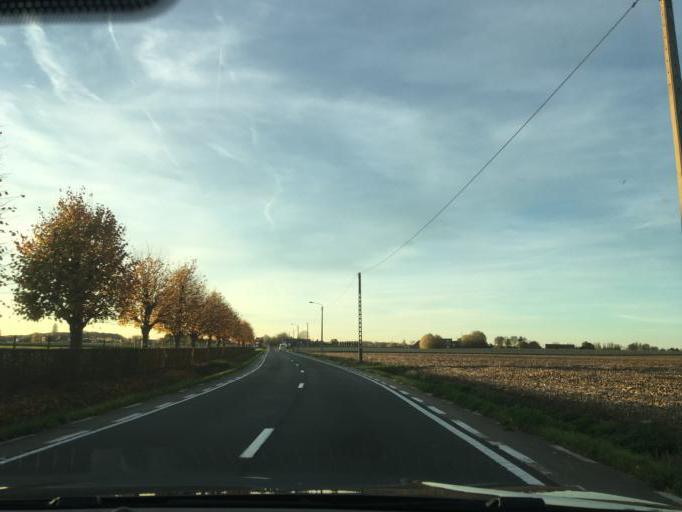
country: BE
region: Flanders
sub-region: Provincie West-Vlaanderen
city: Meulebeke
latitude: 50.9522
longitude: 3.2651
